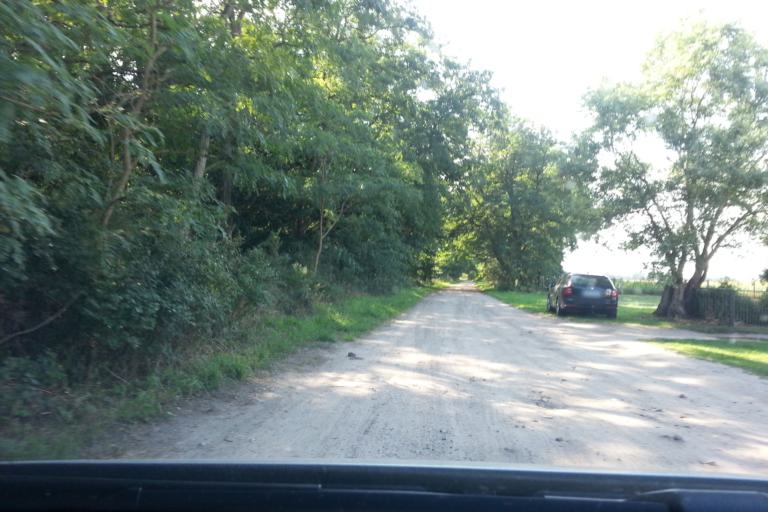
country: DE
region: Mecklenburg-Vorpommern
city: Ferdinandshof
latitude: 53.6405
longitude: 13.8518
